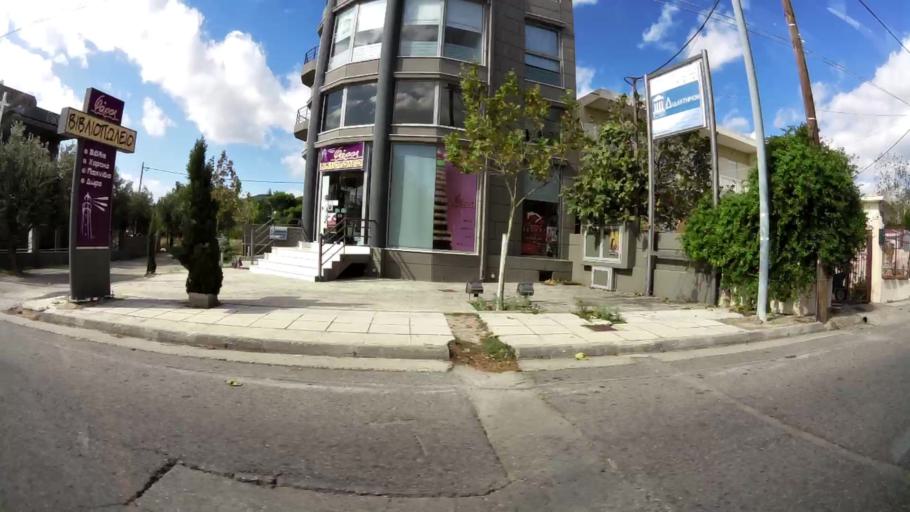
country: GR
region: Attica
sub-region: Nomarchia Anatolikis Attikis
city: Thrakomakedones
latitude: 38.1108
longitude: 23.7439
